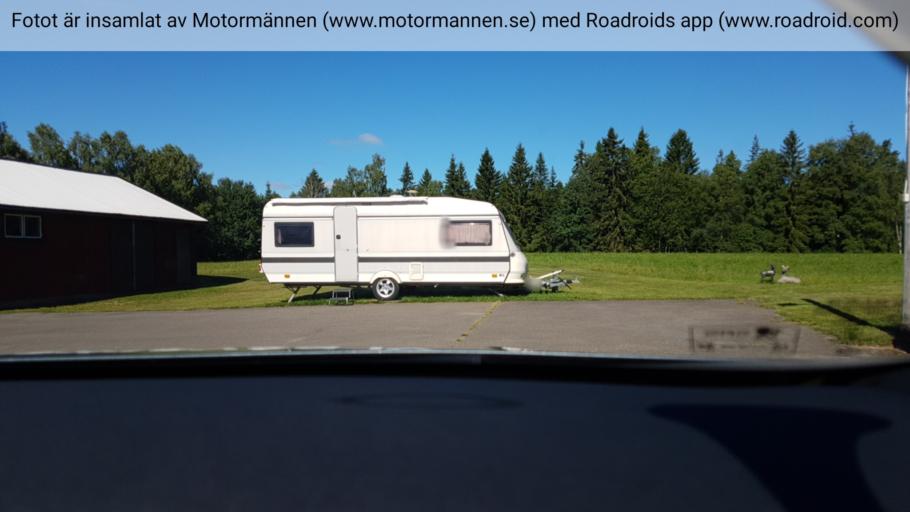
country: SE
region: Vaestra Goetaland
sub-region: Falkopings Kommun
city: Akarp
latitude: 58.2633
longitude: 13.6451
